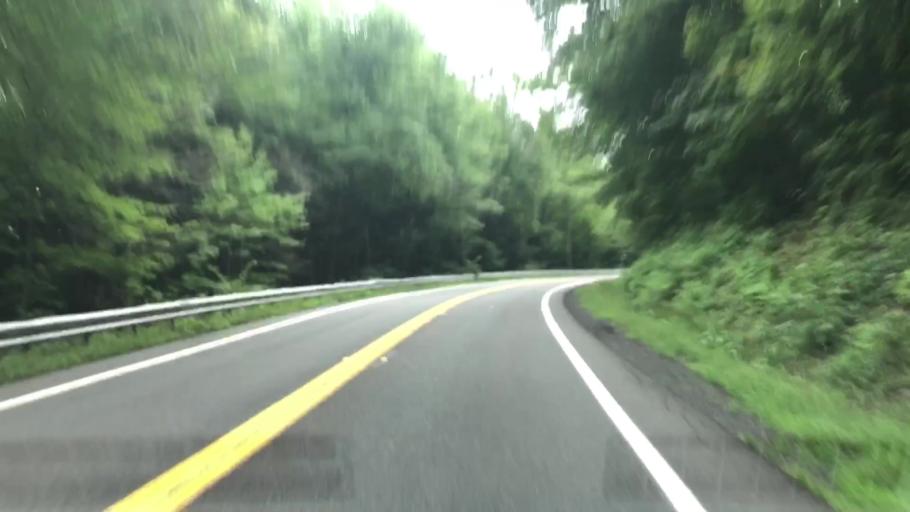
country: US
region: Massachusetts
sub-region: Hampshire County
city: Westhampton
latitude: 42.3071
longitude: -72.8619
